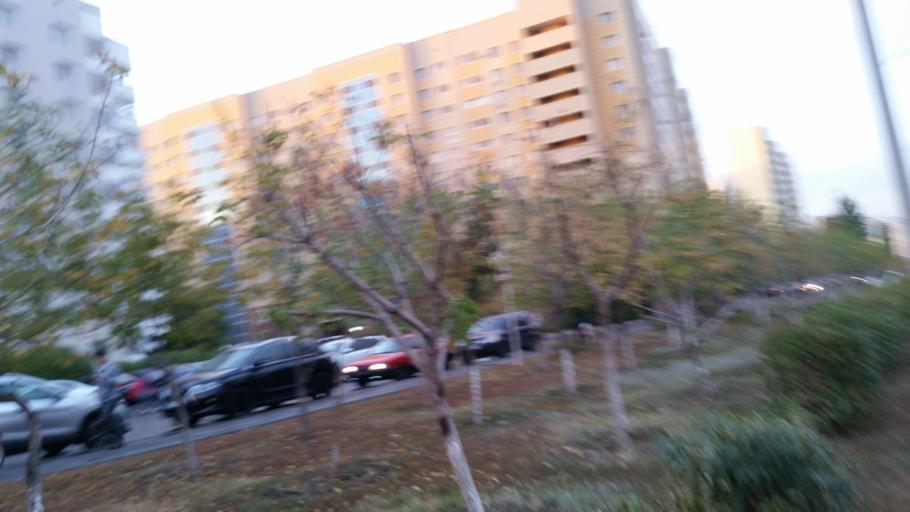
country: KZ
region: Astana Qalasy
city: Astana
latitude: 51.1209
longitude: 71.4206
